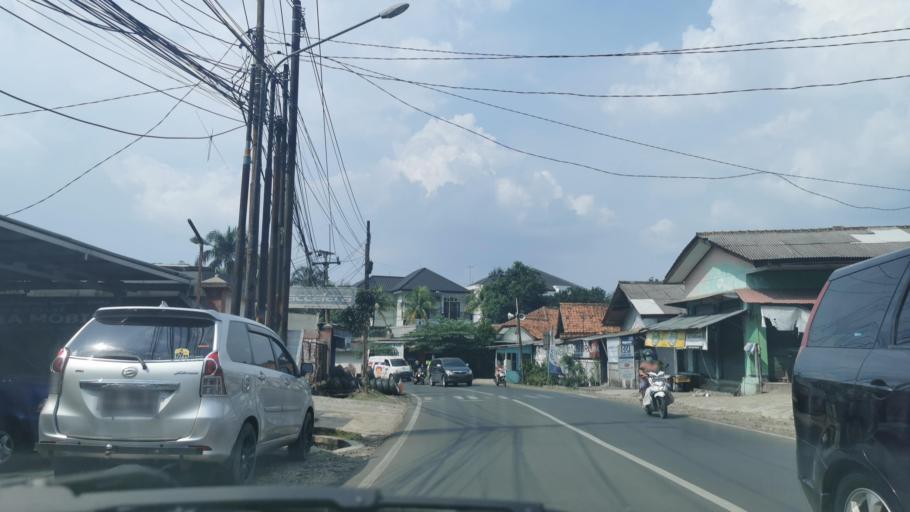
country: ID
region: West Java
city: Depok
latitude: -6.4071
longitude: 106.8358
